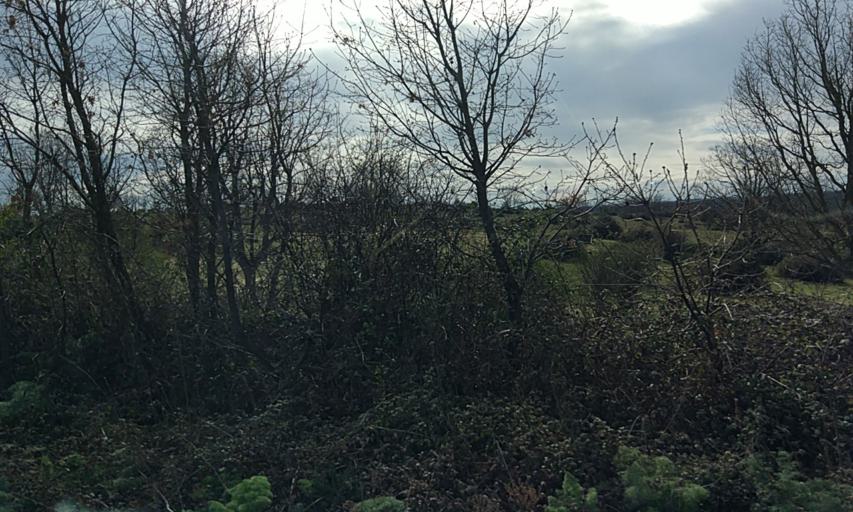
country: ES
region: Castille and Leon
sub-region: Provincia de Salamanca
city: Robleda
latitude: 40.4230
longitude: -6.6015
